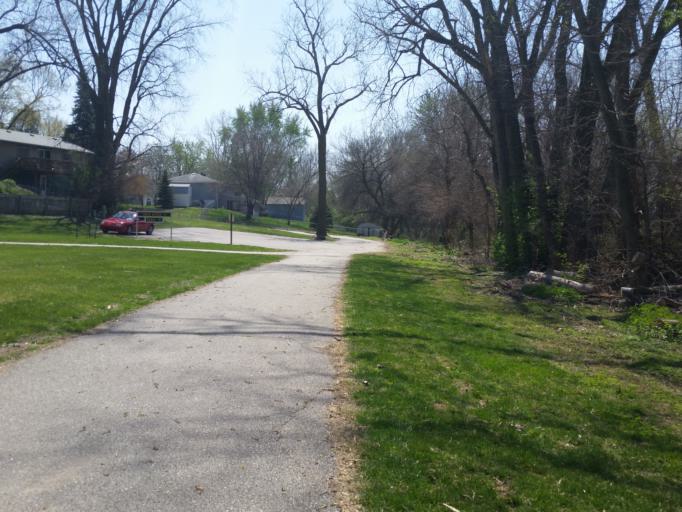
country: US
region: Nebraska
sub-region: Sarpy County
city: Offutt Air Force Base
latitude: 41.1453
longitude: -95.9344
